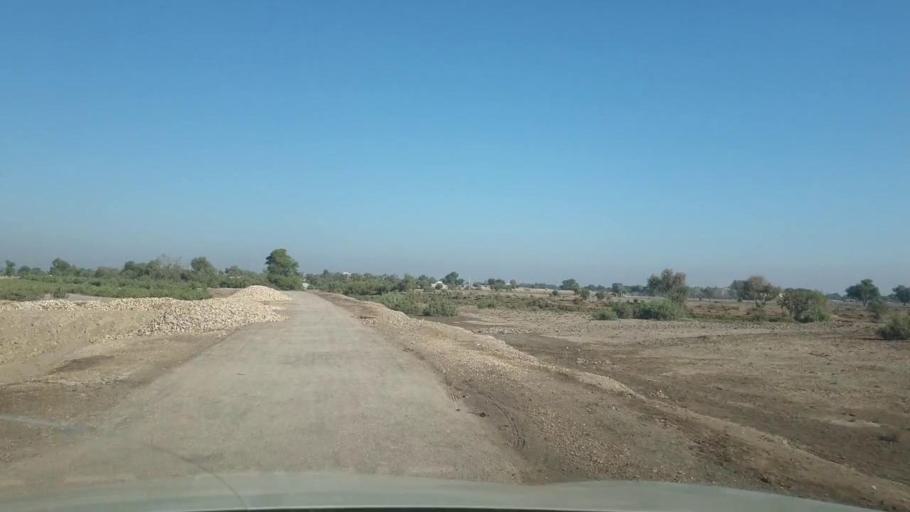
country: PK
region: Sindh
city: Bhan
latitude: 26.5365
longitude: 67.6587
